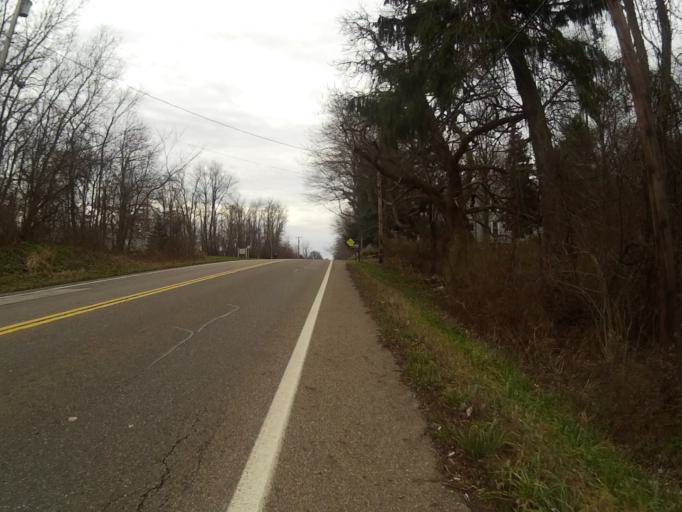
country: US
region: Ohio
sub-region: Summit County
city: Mogadore
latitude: 41.0315
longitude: -81.3474
